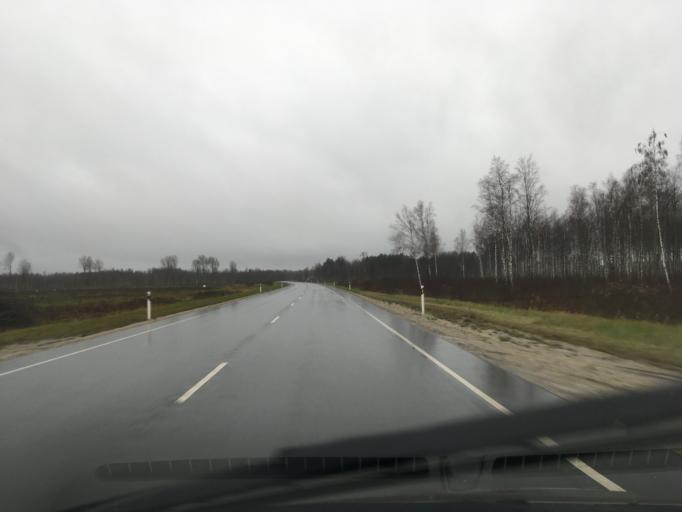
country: EE
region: Harju
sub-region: Nissi vald
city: Turba
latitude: 58.8568
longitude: 24.0716
